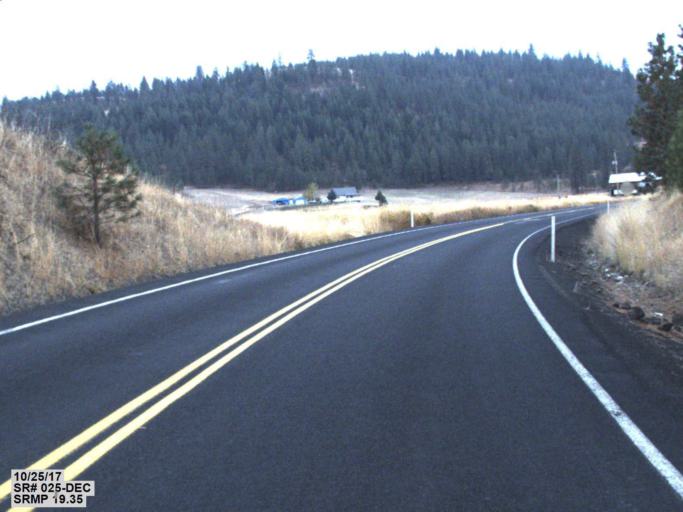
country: US
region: Washington
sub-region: Lincoln County
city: Davenport
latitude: 47.8864
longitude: -118.2644
